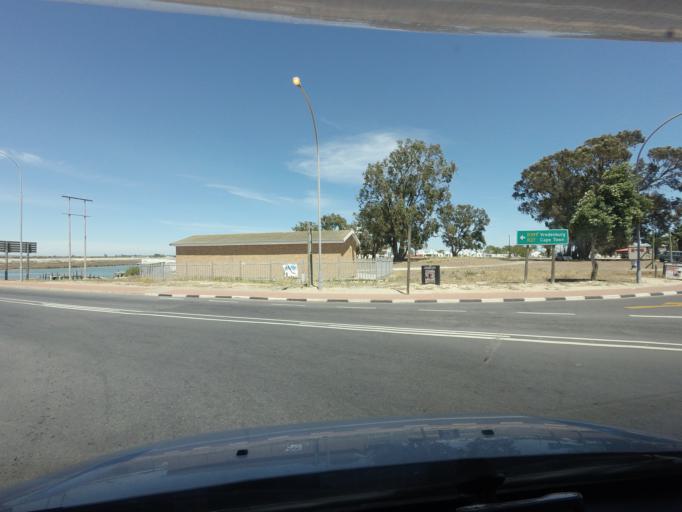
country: ZA
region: Western Cape
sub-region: West Coast District Municipality
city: Vredenburg
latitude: -32.7864
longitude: 18.1691
